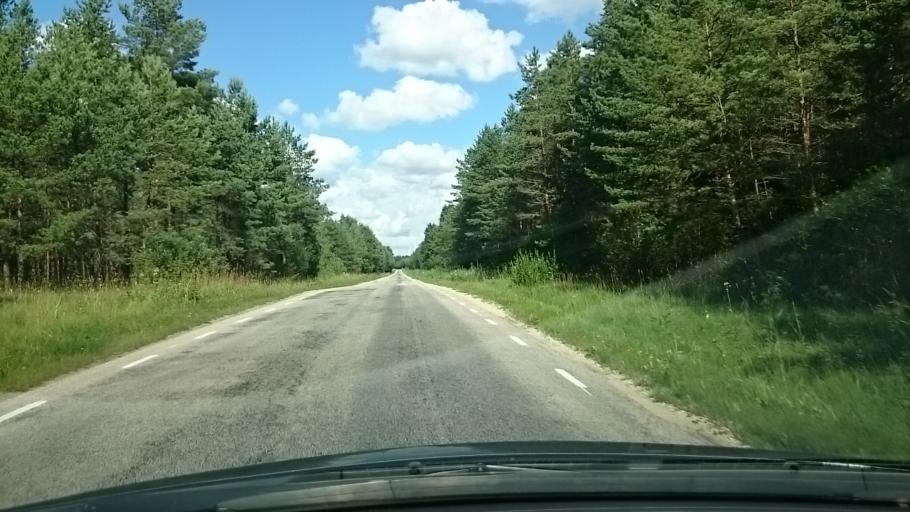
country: EE
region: Laeaene
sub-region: Haapsalu linn
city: Haapsalu
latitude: 59.0619
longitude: 23.5686
